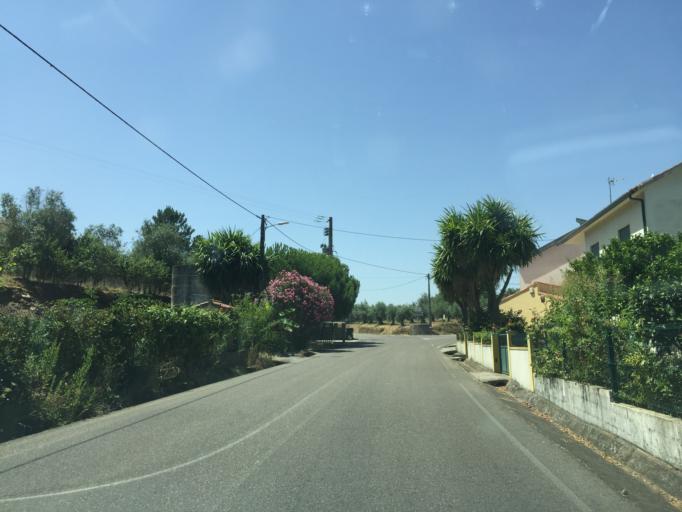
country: PT
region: Santarem
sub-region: Ferreira do Zezere
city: Ferreira do Zezere
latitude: 39.6313
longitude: -8.3083
